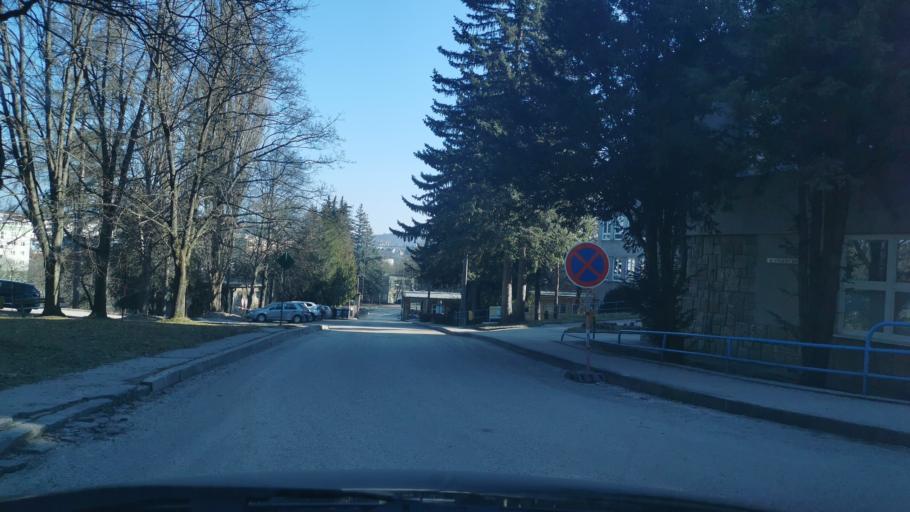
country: SK
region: Trenciansky
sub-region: Okres Myjava
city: Myjava
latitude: 48.7638
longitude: 17.5618
